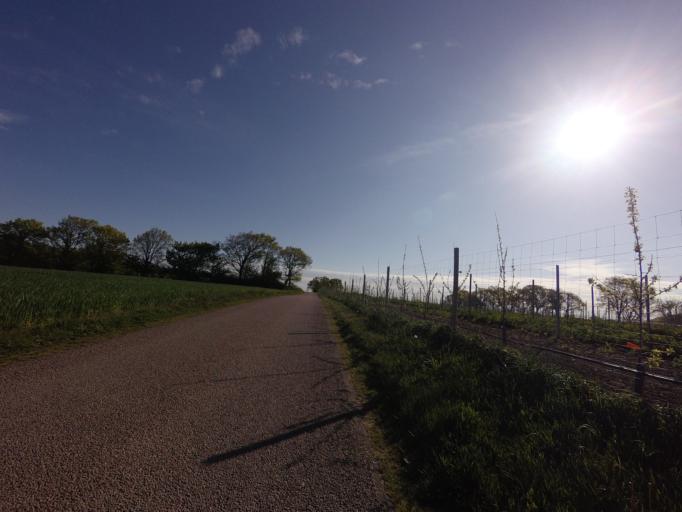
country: SE
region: Skane
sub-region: Hoganas Kommun
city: Hoganas
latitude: 56.2594
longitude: 12.5457
